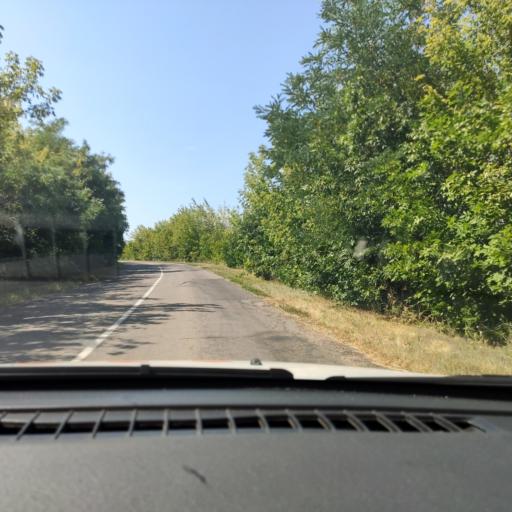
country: RU
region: Voronezj
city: Imeni Pervogo Maya
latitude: 50.7174
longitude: 39.3530
